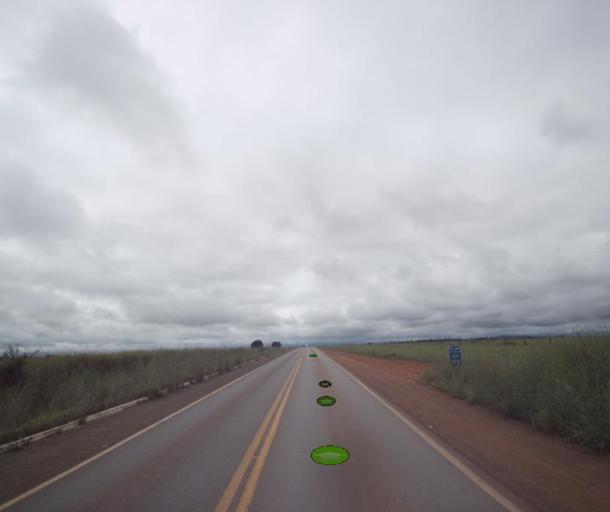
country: BR
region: Goias
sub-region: Uruacu
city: Uruacu
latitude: -14.6898
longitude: -49.1231
